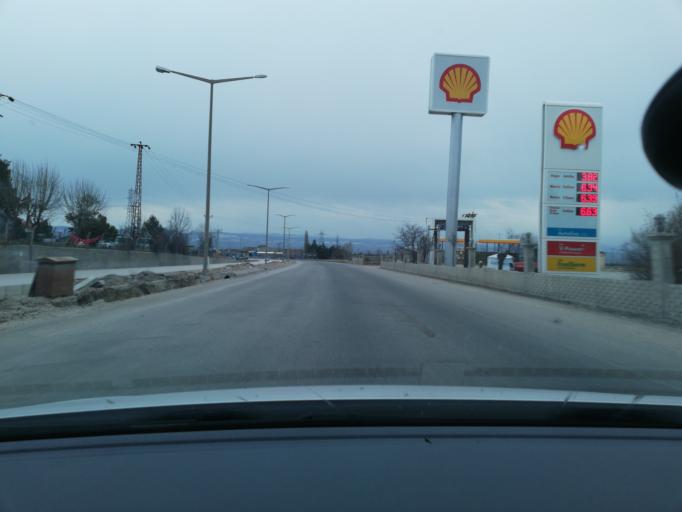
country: TR
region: Bolu
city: Gerede
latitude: 40.7874
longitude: 32.2093
